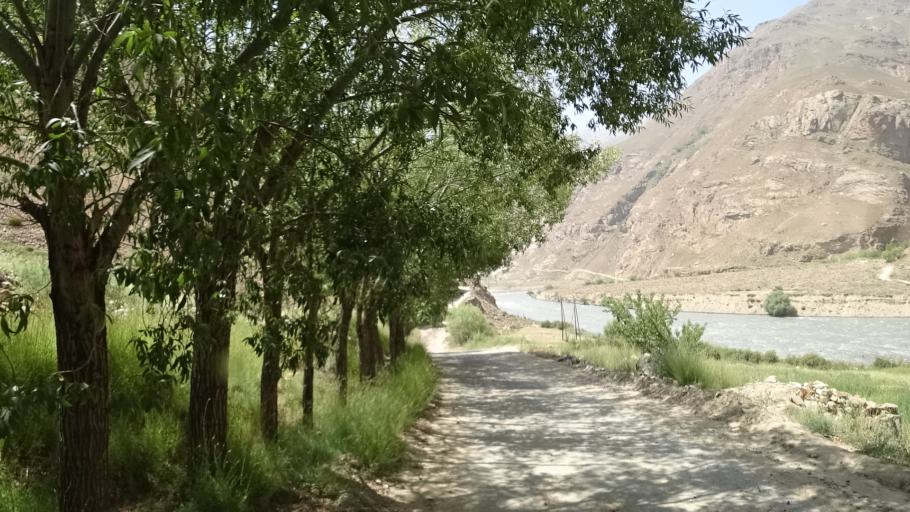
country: TJ
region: Gorno-Badakhshan
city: Khorugh
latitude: 37.1489
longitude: 71.4502
